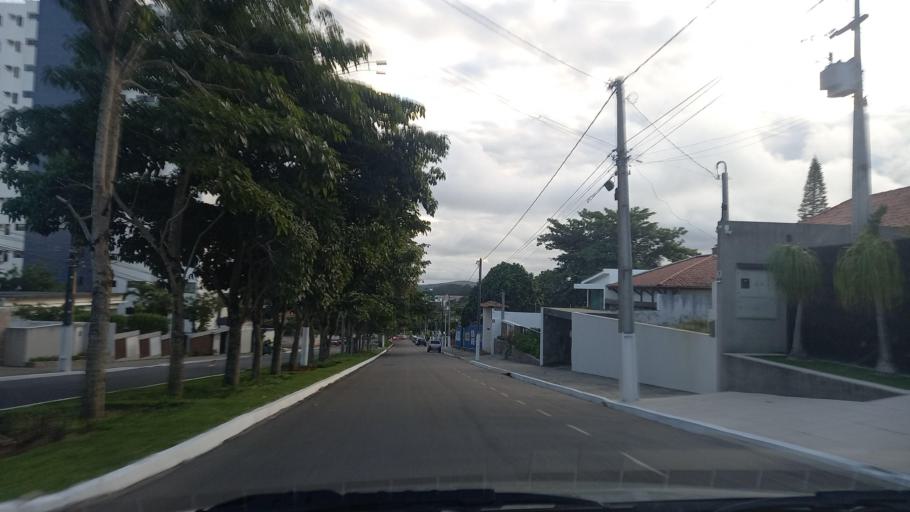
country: BR
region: Pernambuco
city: Garanhuns
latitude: -8.8803
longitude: -36.4737
